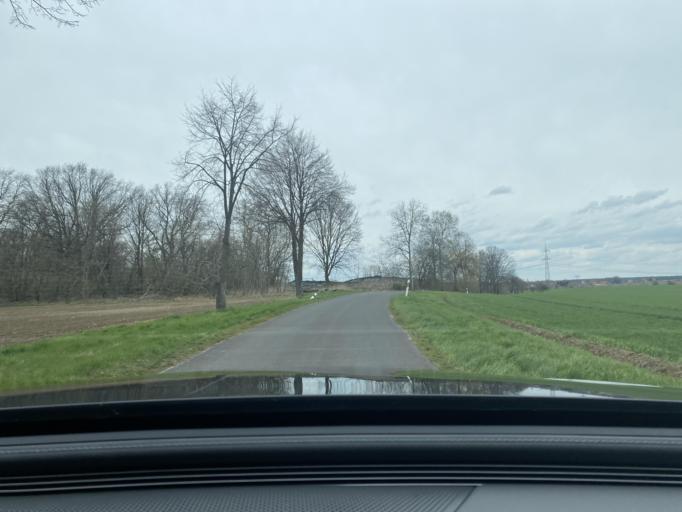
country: DE
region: Saxony
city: Neschwitz
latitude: 51.2322
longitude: 14.3411
